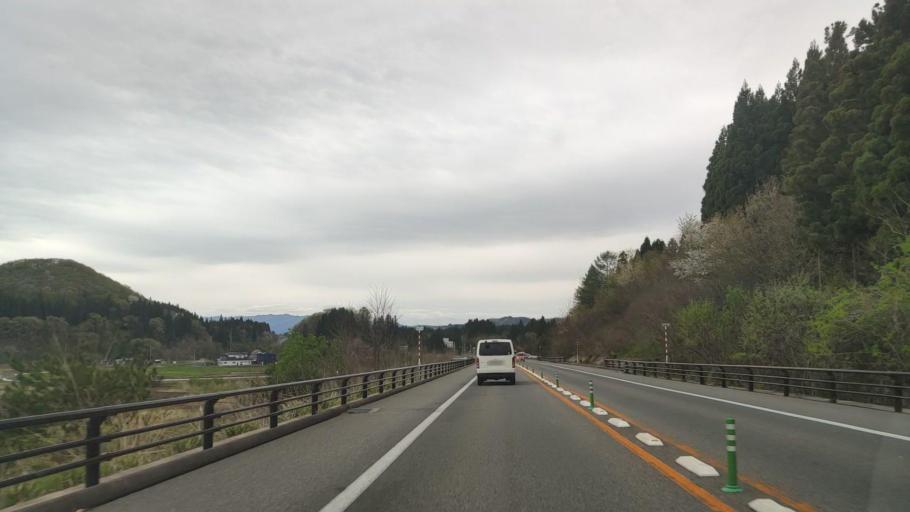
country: JP
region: Akita
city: Odate
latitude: 40.3173
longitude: 140.5856
